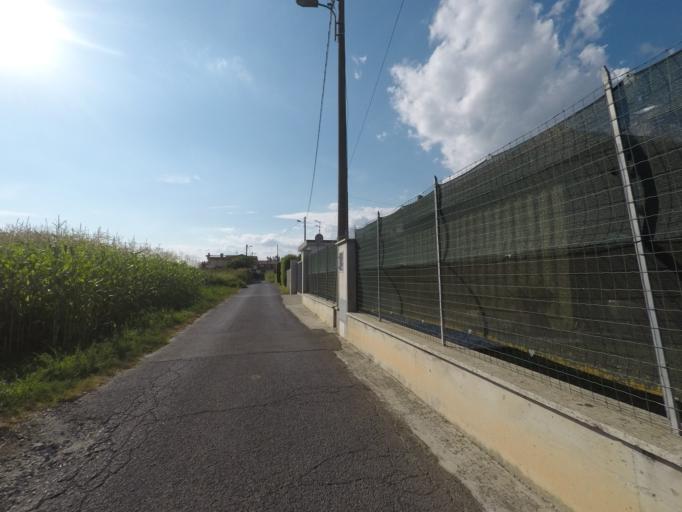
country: IT
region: Tuscany
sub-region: Provincia di Massa-Carrara
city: Capanne-Prato-Cinquale
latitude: 44.0131
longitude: 10.1452
